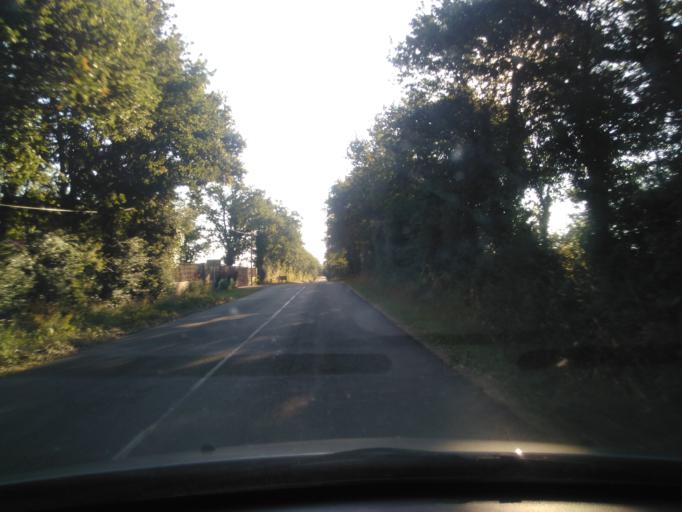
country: FR
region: Pays de la Loire
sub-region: Departement de la Vendee
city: Mouilleron-le-Captif
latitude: 46.7343
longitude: -1.4228
